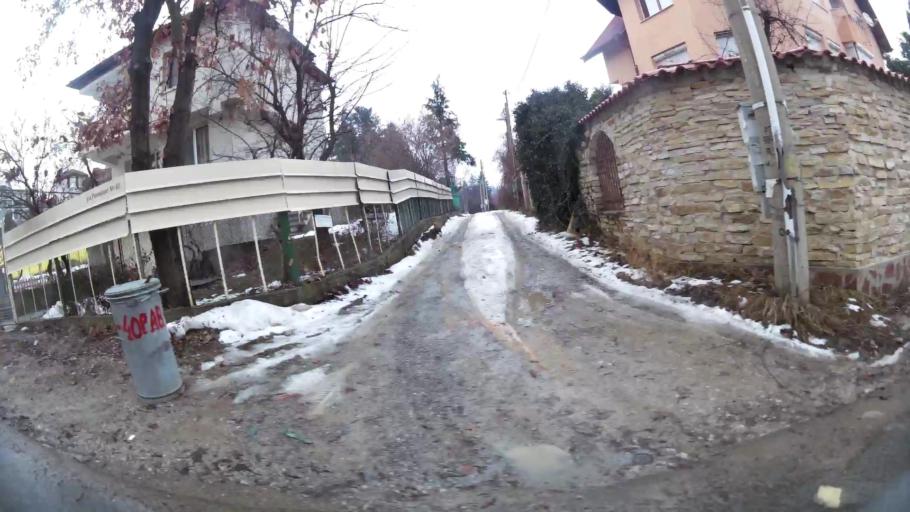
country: BG
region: Sofiya
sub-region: Obshtina Bozhurishte
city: Bozhurishte
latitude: 42.6717
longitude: 23.2312
